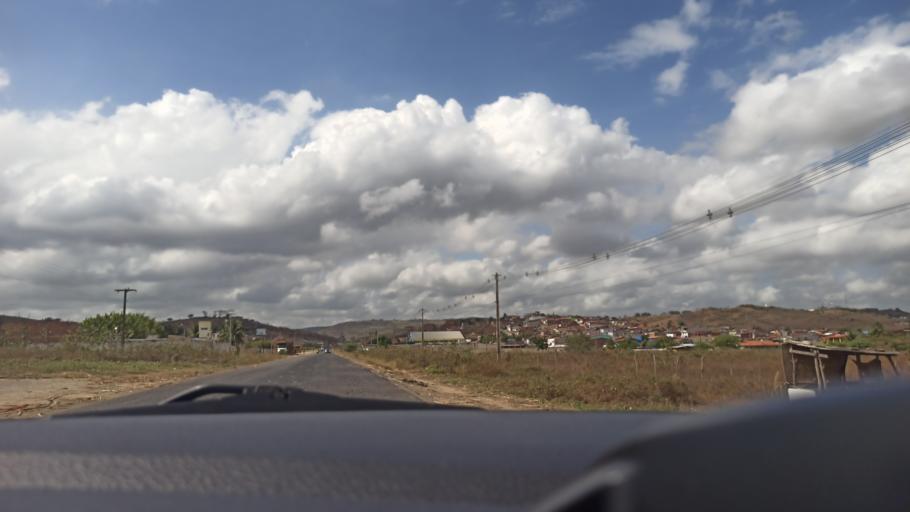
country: BR
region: Pernambuco
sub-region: Timbauba
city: Timbauba
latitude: -7.4968
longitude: -35.2978
